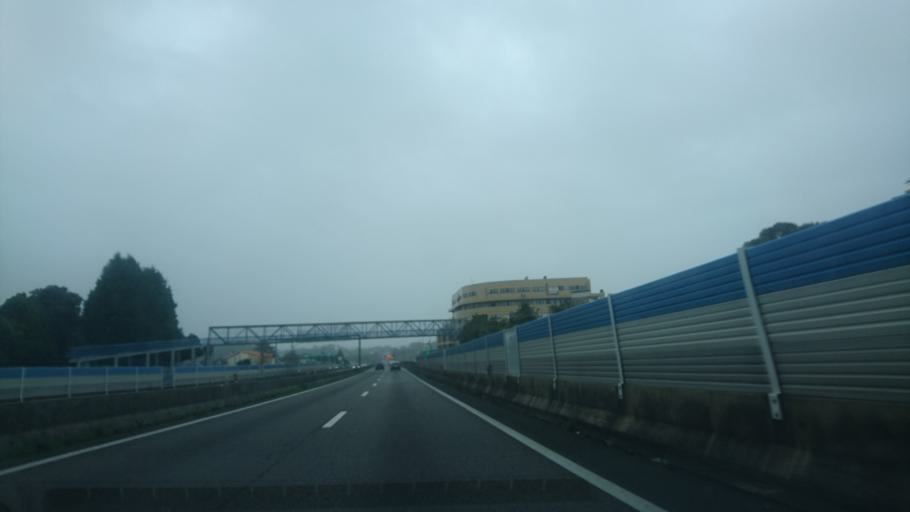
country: PT
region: Porto
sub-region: Vila Nova de Gaia
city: Vilar do Paraiso
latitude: 41.0958
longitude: -8.6284
